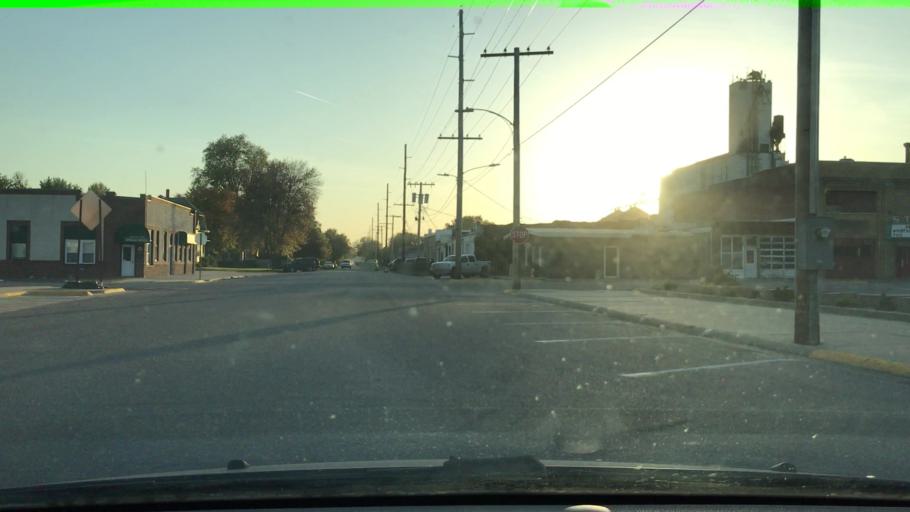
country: US
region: Nebraska
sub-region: Merrick County
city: Central City
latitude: 41.1149
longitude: -98.0021
